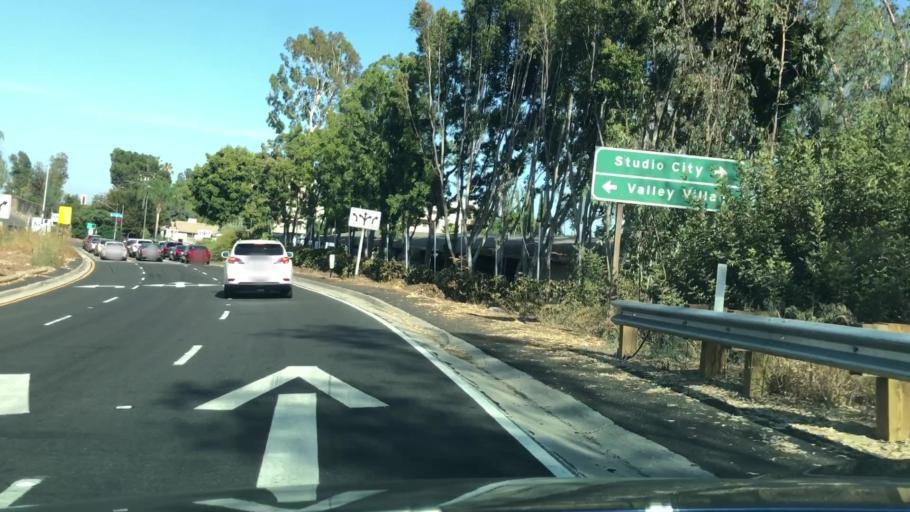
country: US
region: California
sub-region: Los Angeles County
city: North Hollywood
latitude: 34.1539
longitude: -118.3979
